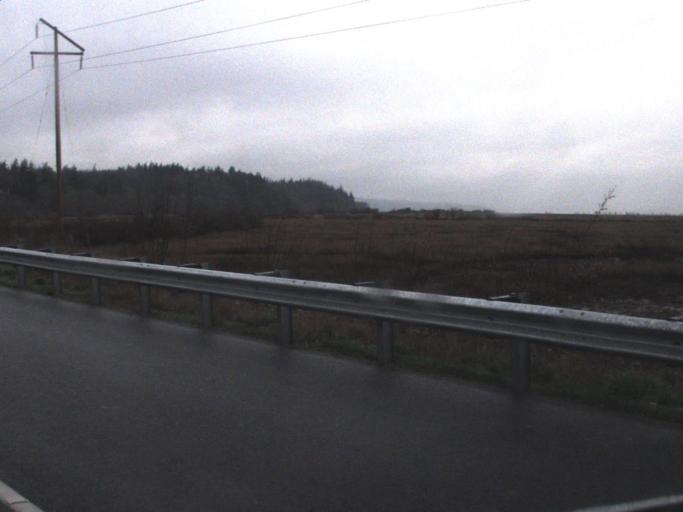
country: US
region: Washington
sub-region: Snohomish County
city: Stanwood
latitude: 48.2398
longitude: -122.3922
